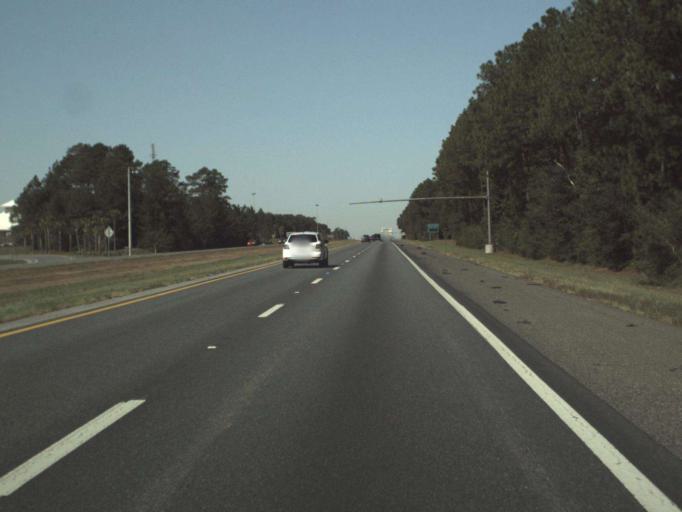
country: US
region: Florida
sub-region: Escambia County
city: Cantonment
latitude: 30.5433
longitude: -87.3471
